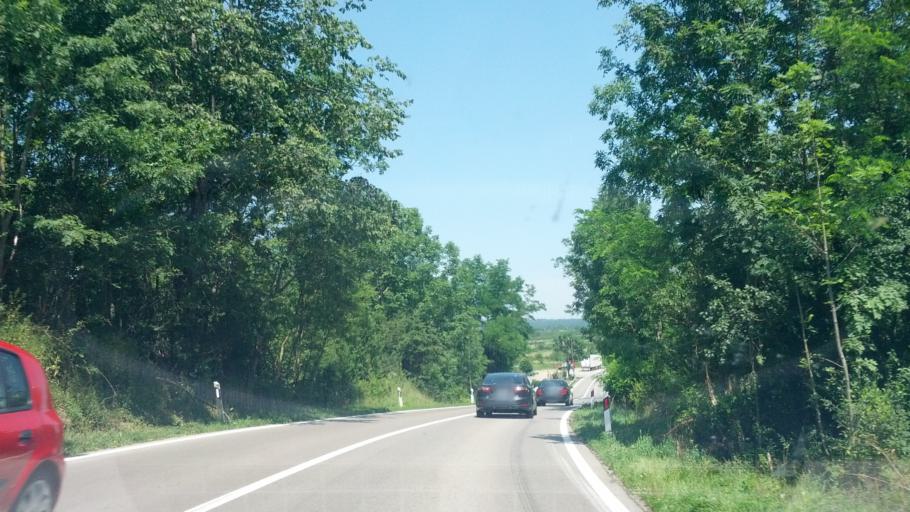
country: BA
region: Federation of Bosnia and Herzegovina
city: Izacic
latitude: 44.8885
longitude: 15.7258
